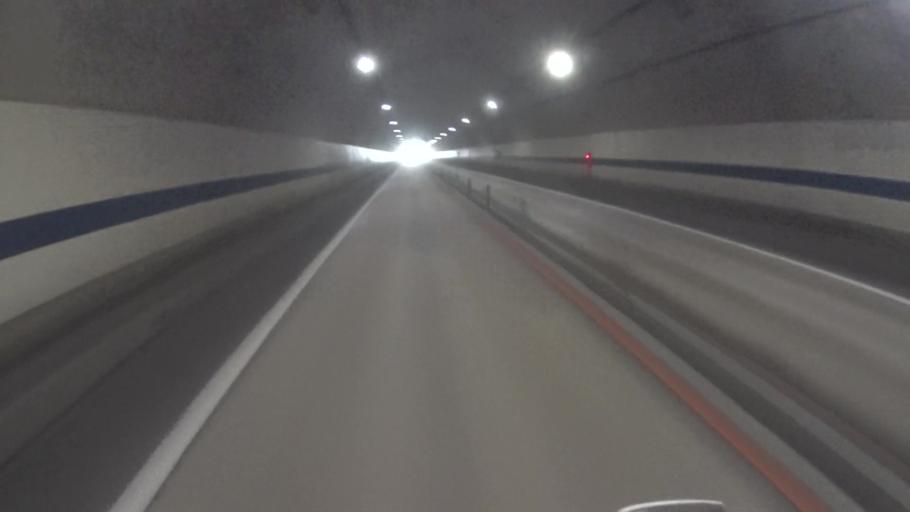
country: JP
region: Kyoto
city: Maizuru
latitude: 35.4137
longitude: 135.2225
